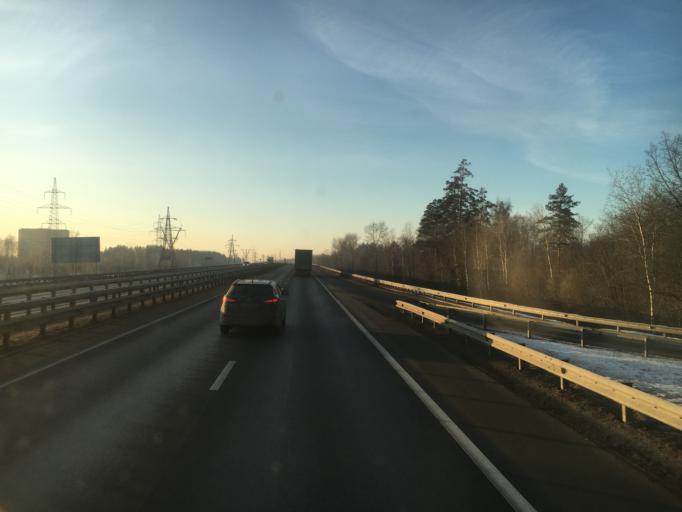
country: RU
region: Samara
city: Pribrezhnyy
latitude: 53.5174
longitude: 49.8405
